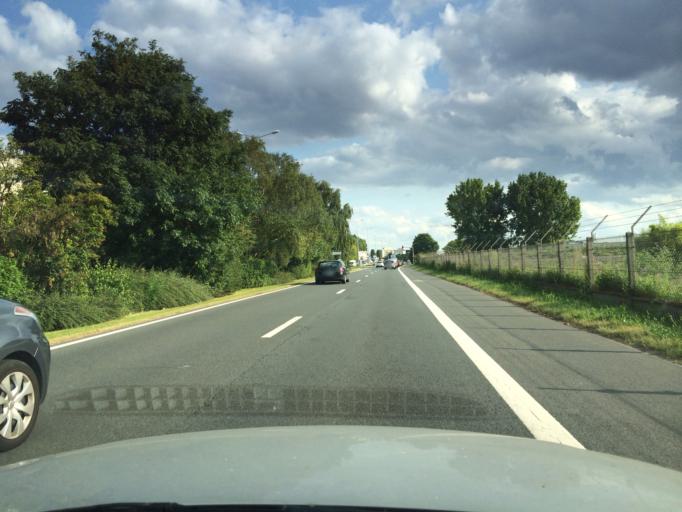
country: FR
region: Lower Normandy
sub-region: Departement du Calvados
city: Epron
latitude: 49.2078
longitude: -0.3623
